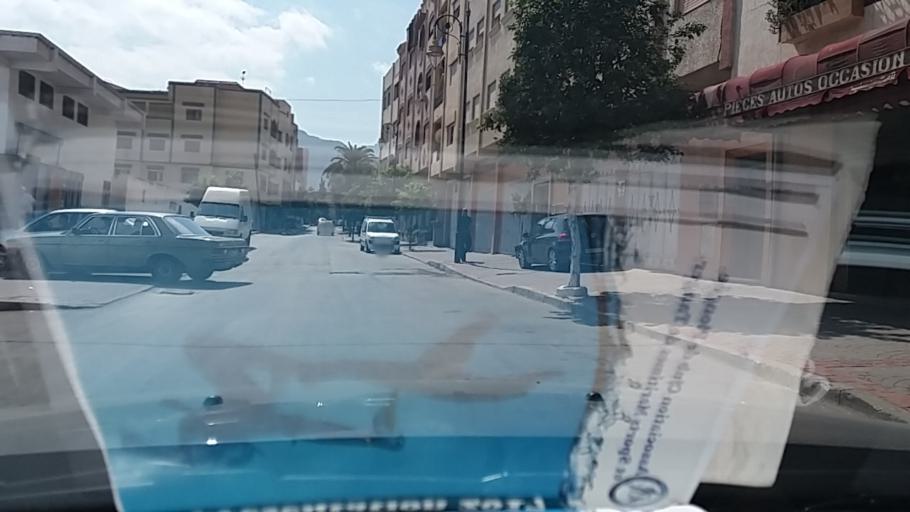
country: MA
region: Tanger-Tetouan
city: Tetouan
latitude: 35.5697
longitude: -5.3557
